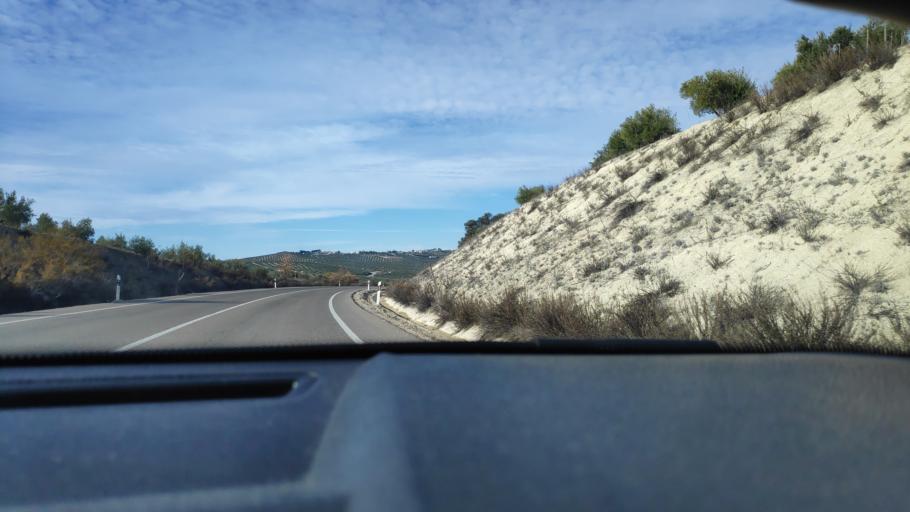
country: ES
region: Andalusia
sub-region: Provincia de Jaen
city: Porcuna
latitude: 37.8528
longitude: -4.1428
